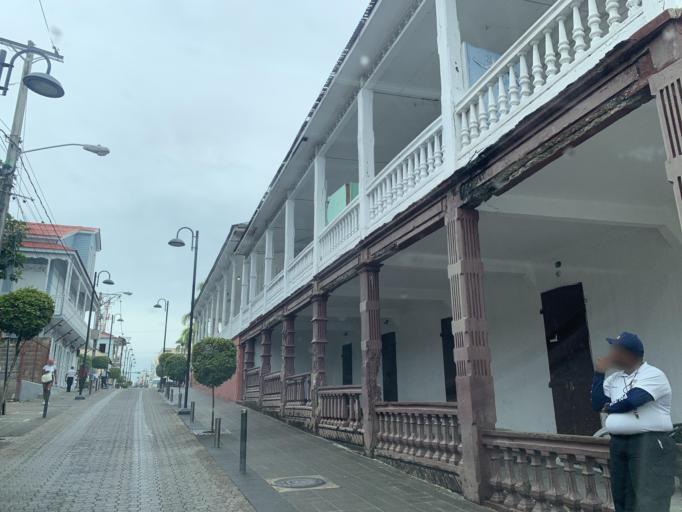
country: DO
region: Puerto Plata
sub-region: Puerto Plata
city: Puerto Plata
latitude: 19.7983
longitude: -70.6938
